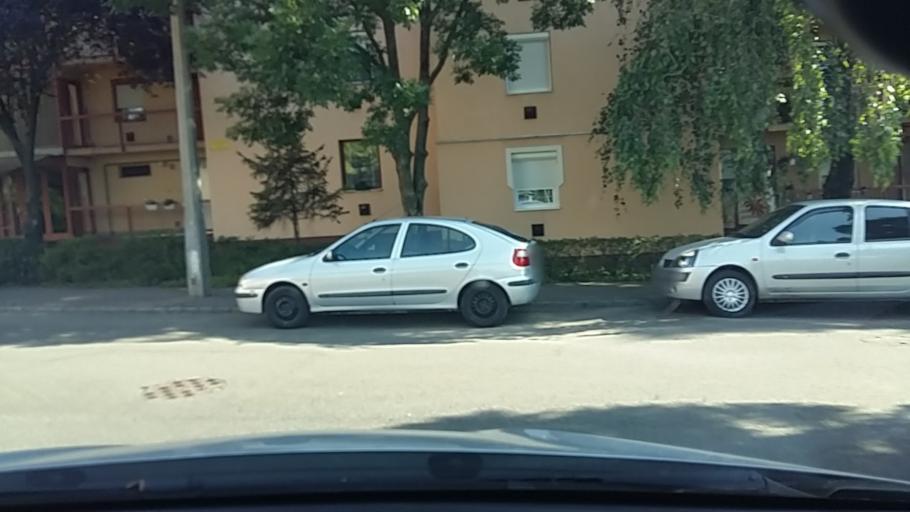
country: HU
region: Heves
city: Gyongyos
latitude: 47.7787
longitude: 19.9119
